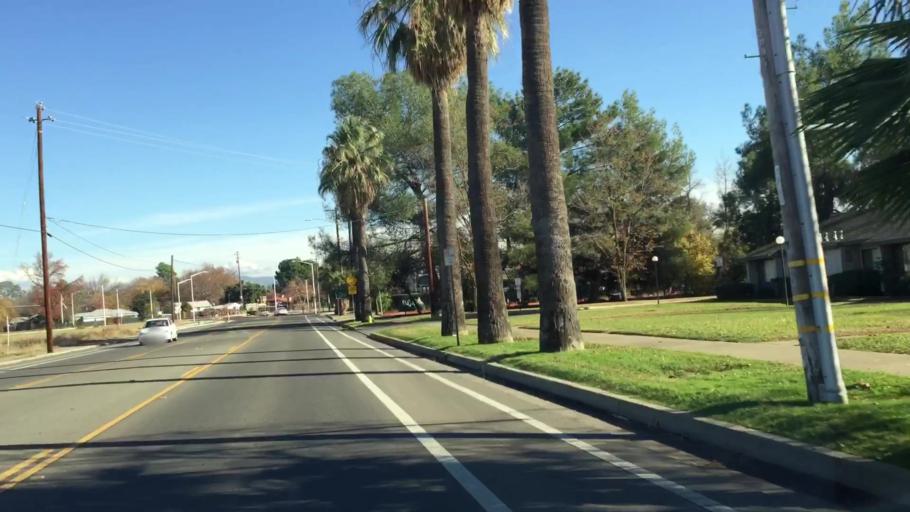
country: US
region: California
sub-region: Butte County
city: Oroville
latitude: 39.5240
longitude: -121.5615
